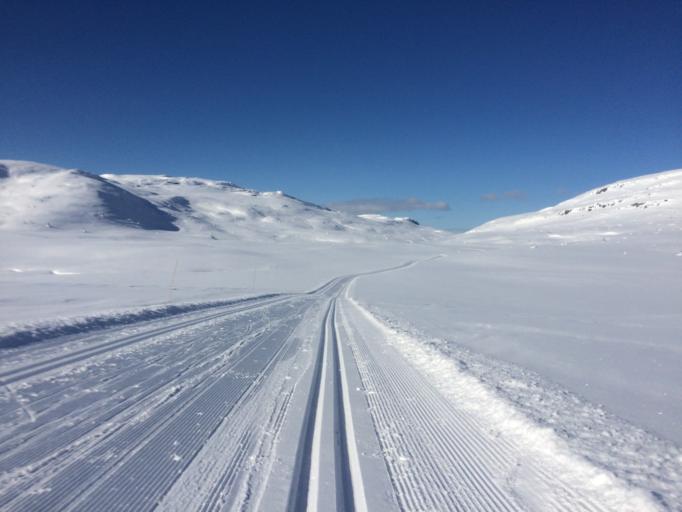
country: NO
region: Oppland
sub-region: Ringebu
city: Ringebu
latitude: 61.3793
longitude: 10.0610
